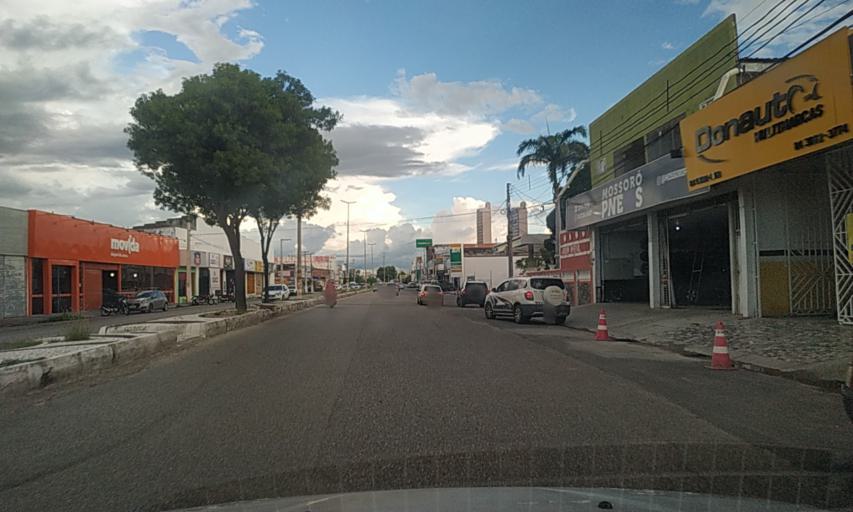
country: BR
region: Rio Grande do Norte
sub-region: Mossoro
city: Mossoro
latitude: -5.1974
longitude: -37.3409
